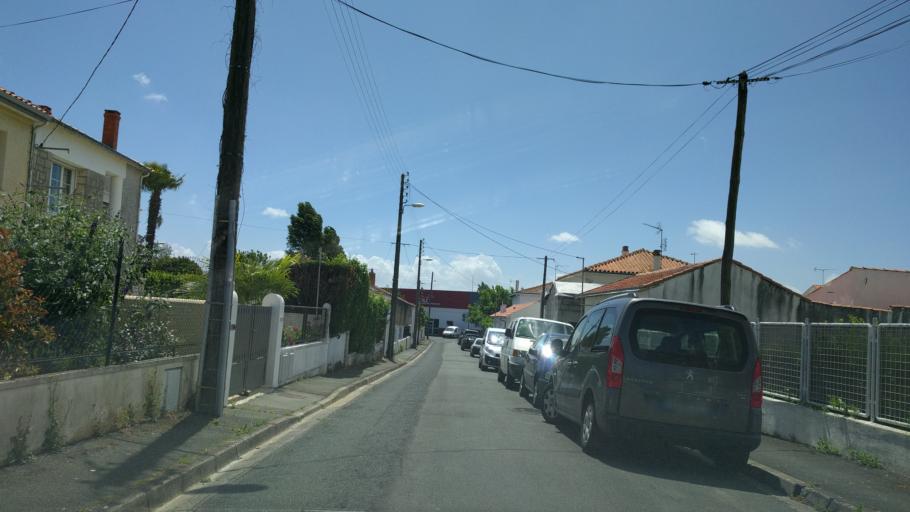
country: FR
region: Poitou-Charentes
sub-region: Departement de la Charente-Maritime
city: La Rochelle
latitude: 46.1624
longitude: -1.1327
